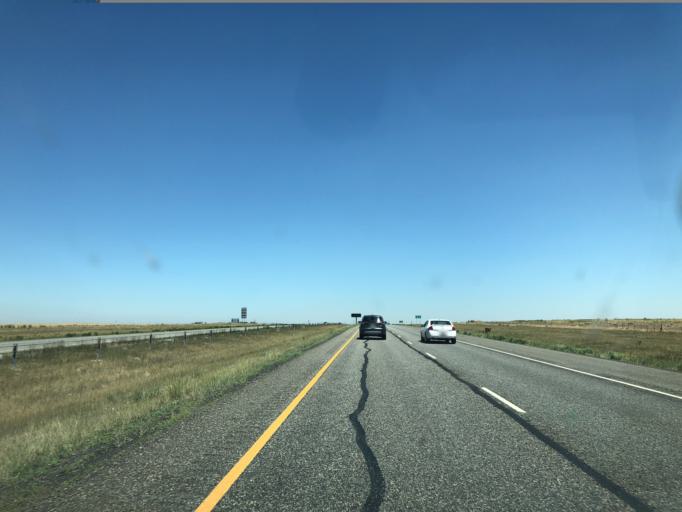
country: US
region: Colorado
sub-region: Adams County
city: Aurora
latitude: 39.7871
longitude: -104.7162
